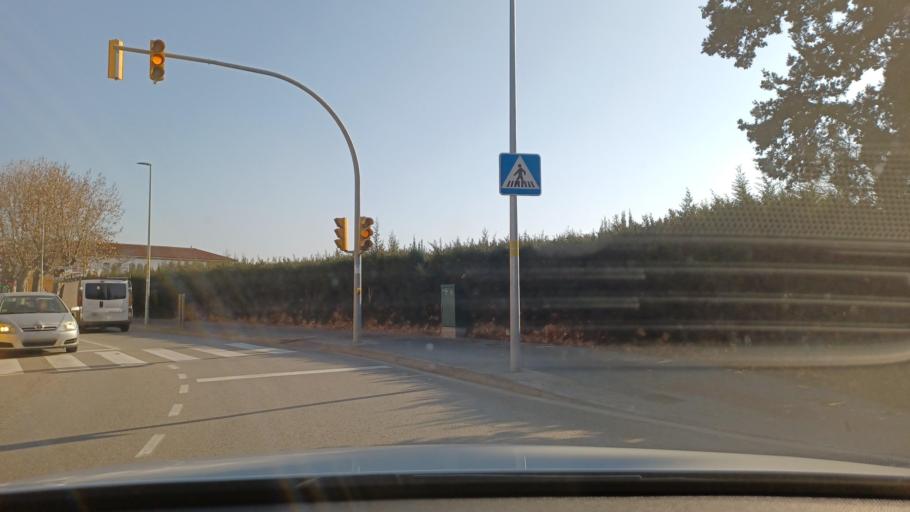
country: ES
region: Catalonia
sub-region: Provincia de Barcelona
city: L'Ametlla del Valles
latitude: 41.6655
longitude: 2.2625
